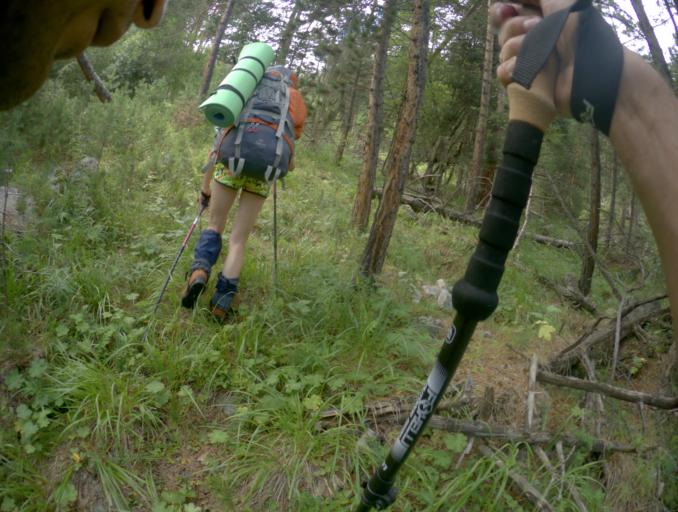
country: RU
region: Karachayevo-Cherkesiya
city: Uchkulan
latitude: 43.3496
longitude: 42.1535
